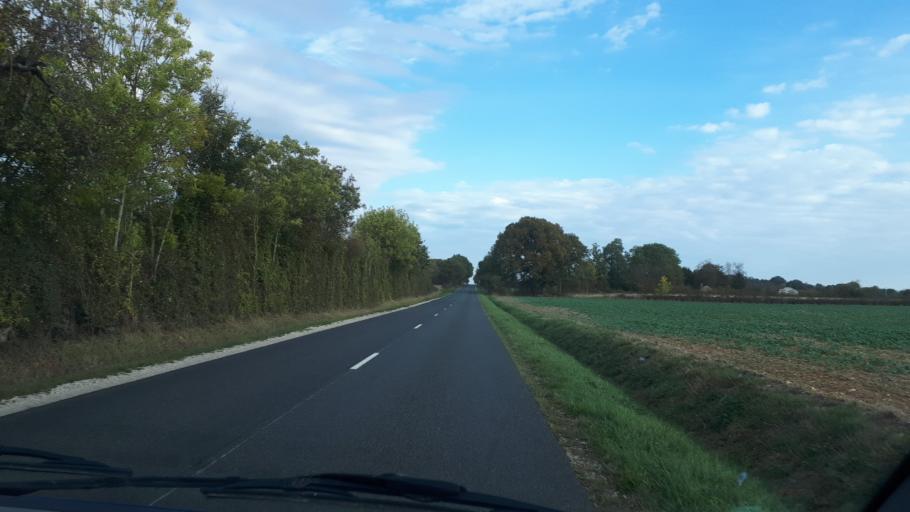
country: FR
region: Centre
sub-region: Departement du Loir-et-Cher
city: Mondoubleau
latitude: 47.9378
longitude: 0.9333
